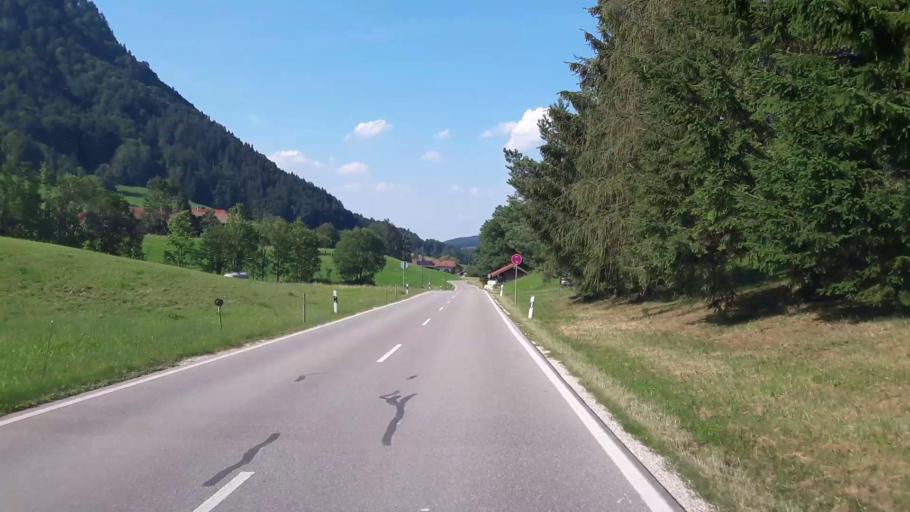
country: DE
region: Bavaria
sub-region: Upper Bavaria
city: Ruhpolding
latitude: 47.7550
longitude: 12.6312
